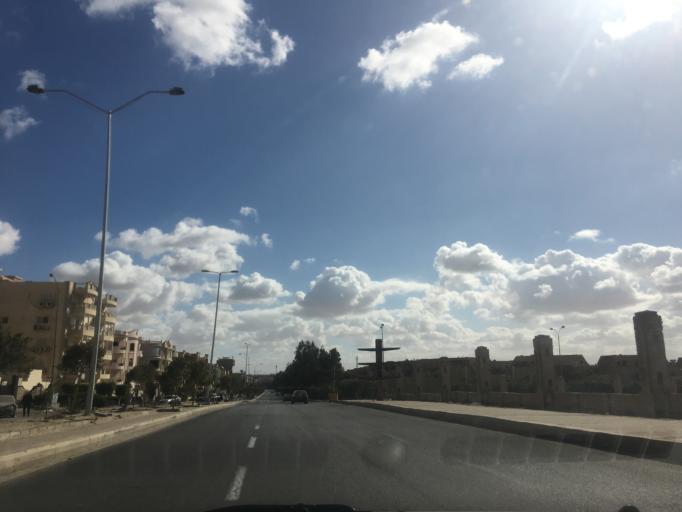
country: EG
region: Al Jizah
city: Madinat Sittah Uktubar
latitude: 29.9999
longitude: 30.9746
